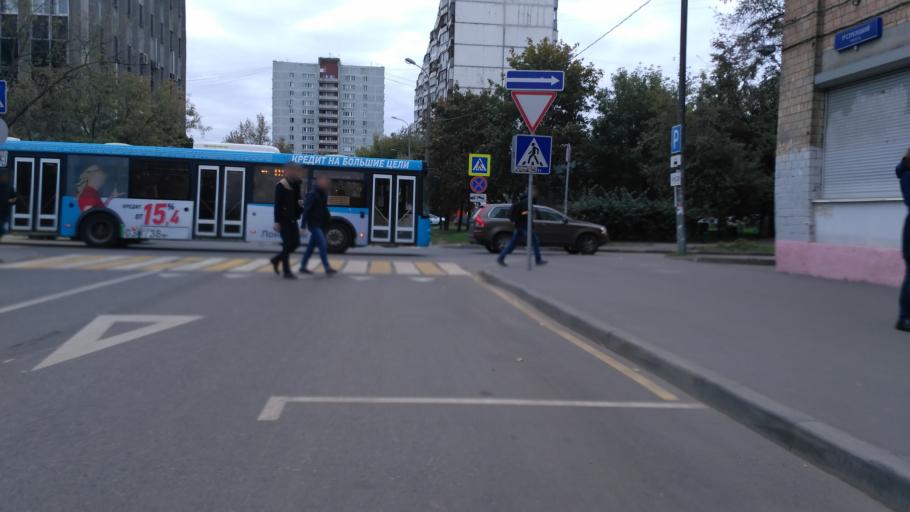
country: RU
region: Moscow
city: Mar'ina Roshcha
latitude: 55.7985
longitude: 37.6083
